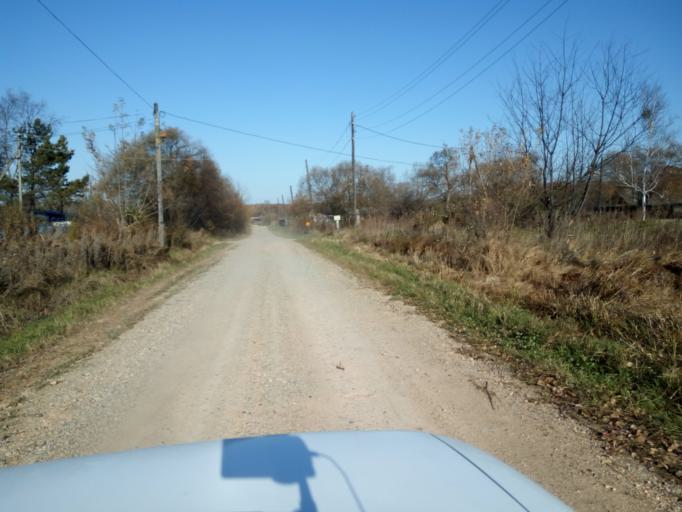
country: RU
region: Primorskiy
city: Lazo
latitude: 45.8754
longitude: 133.6586
